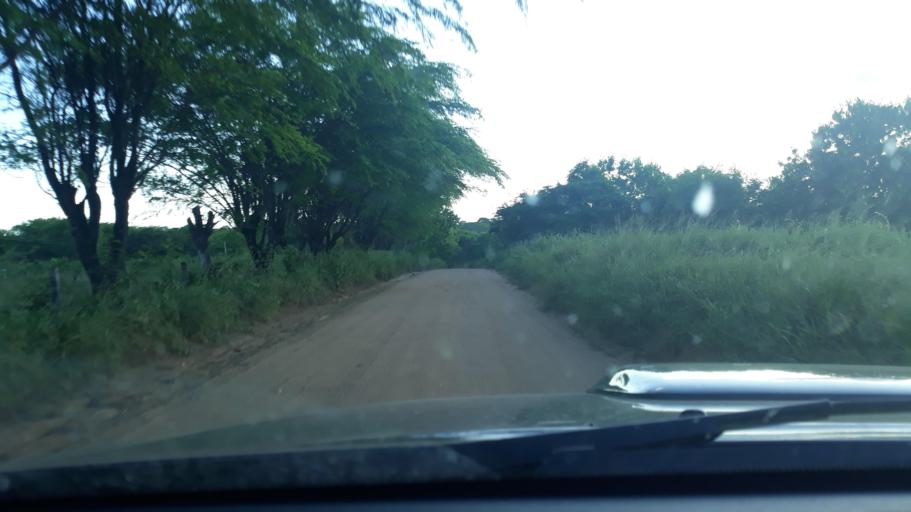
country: BR
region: Bahia
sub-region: Riacho De Santana
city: Riacho de Santana
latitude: -13.8108
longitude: -42.7197
